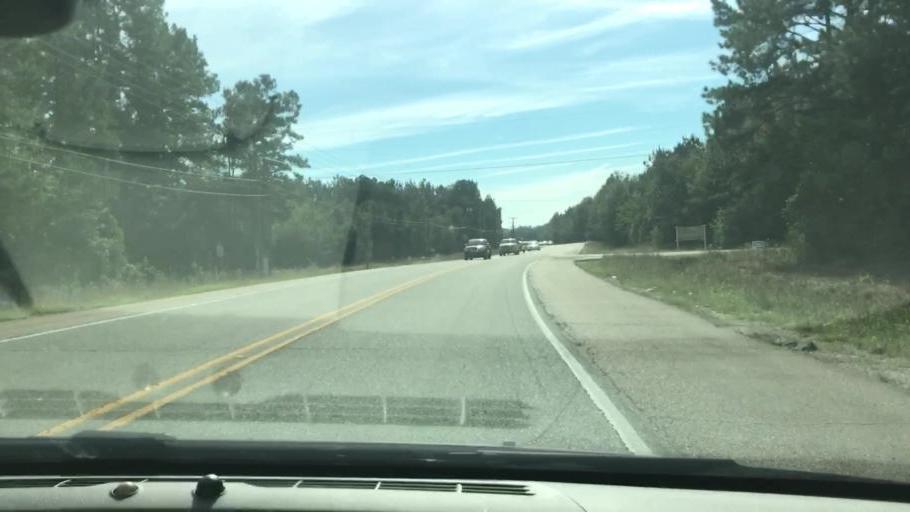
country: US
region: Louisiana
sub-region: Saint Tammany Parish
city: Pearl River
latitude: 30.3981
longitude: -89.7626
